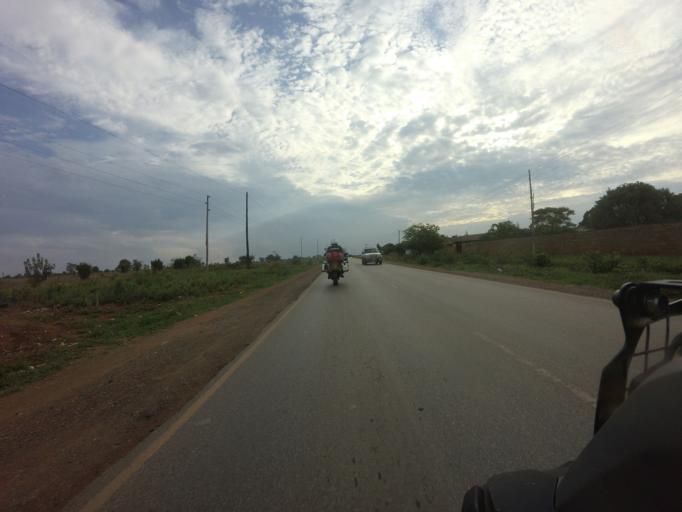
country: ZM
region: Lusaka
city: Lusaka
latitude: -15.4910
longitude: 28.2493
